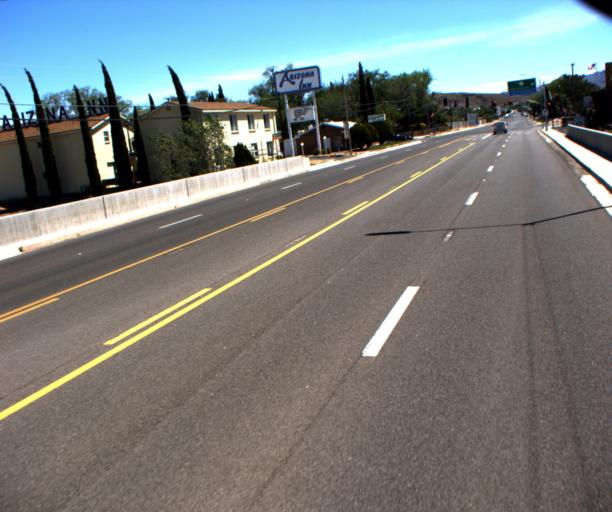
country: US
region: Arizona
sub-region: Mohave County
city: Kingman
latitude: 35.1904
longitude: -114.0627
